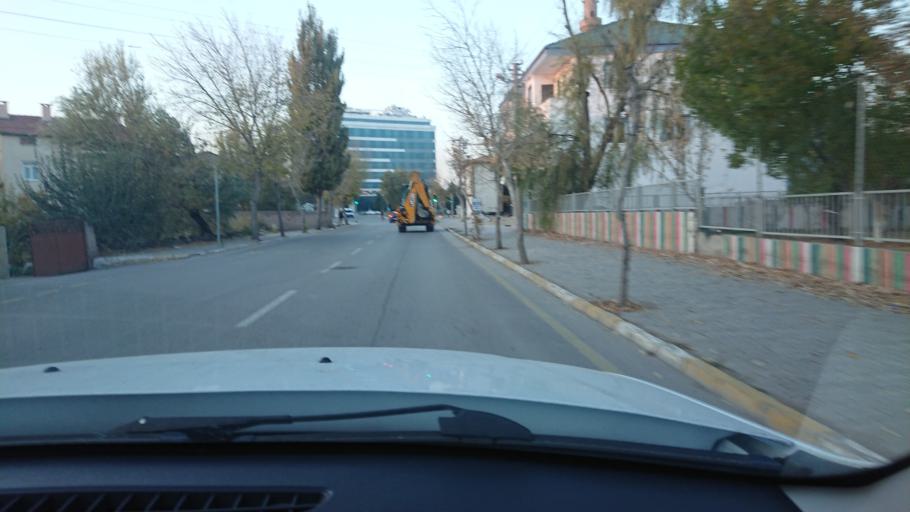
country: TR
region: Aksaray
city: Aksaray
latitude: 38.3569
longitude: 34.0413
